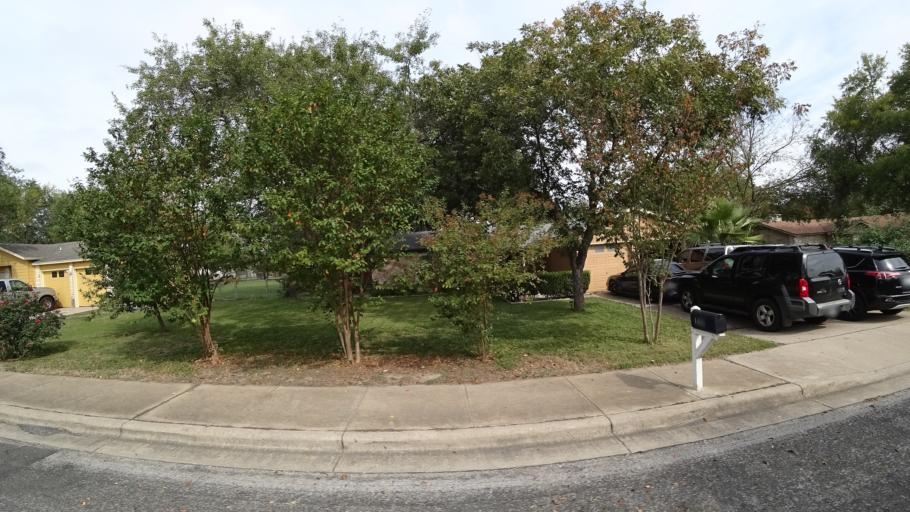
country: US
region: Texas
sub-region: Travis County
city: Wells Branch
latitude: 30.4452
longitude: -97.6621
